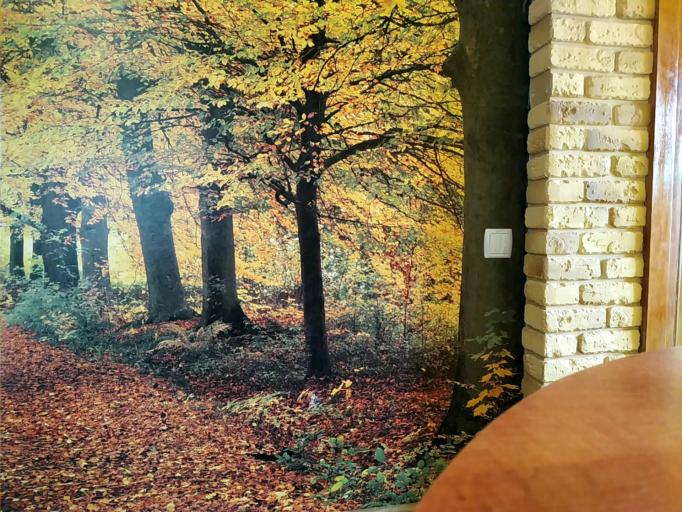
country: RU
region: Leningrad
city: Volosovo
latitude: 59.0294
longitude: 29.2924
